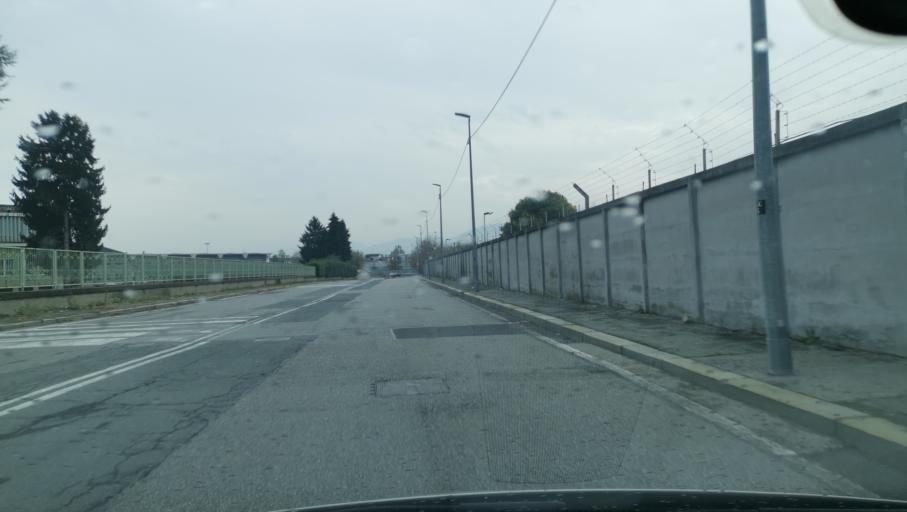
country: IT
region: Piedmont
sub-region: Provincia di Torino
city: Turin
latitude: 45.1150
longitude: 7.7128
